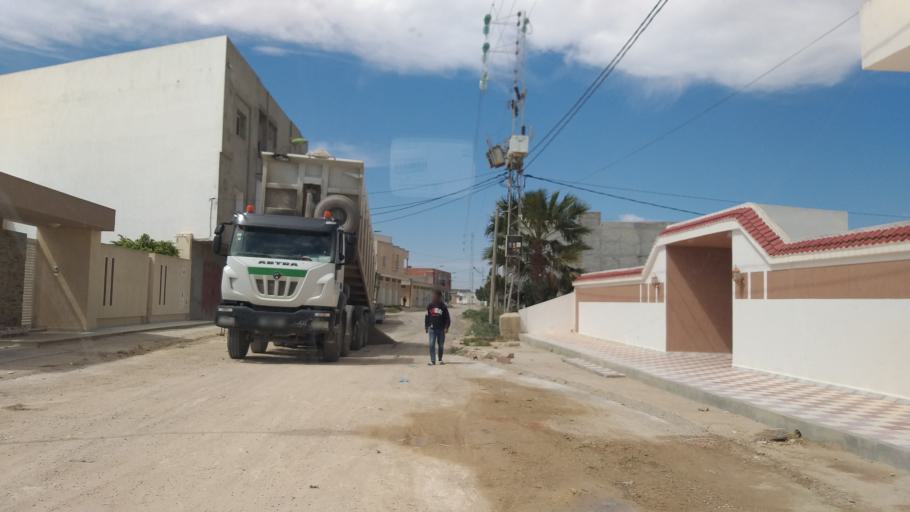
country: TN
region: Al Mahdiyah
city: El Jem
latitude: 35.3035
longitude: 10.6957
